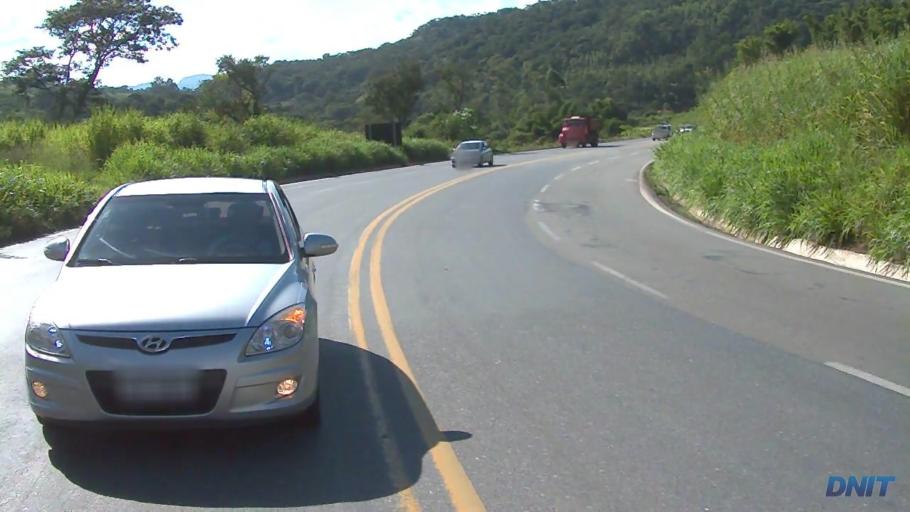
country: BR
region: Minas Gerais
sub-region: Barao De Cocais
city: Barao de Cocais
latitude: -19.8354
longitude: -43.3732
